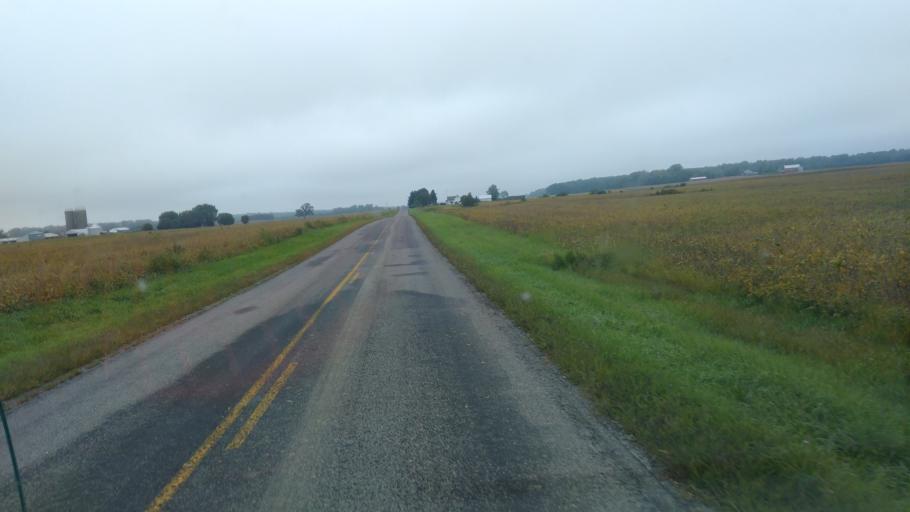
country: US
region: Ohio
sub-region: Hardin County
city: Kenton
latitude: 40.5435
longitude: -83.6341
